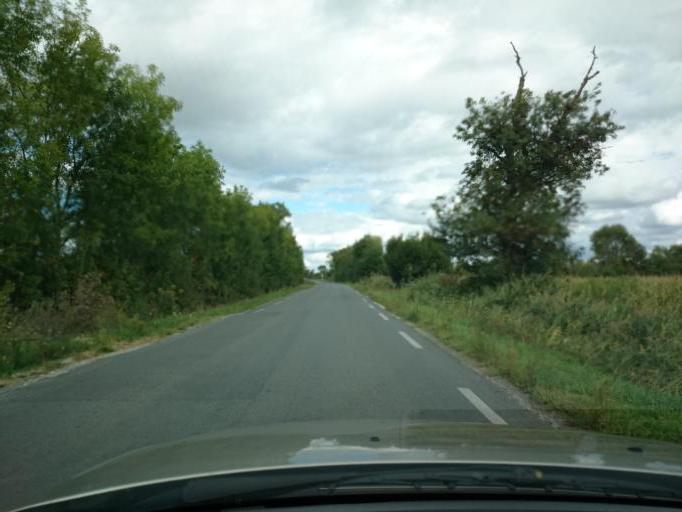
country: FR
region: Aquitaine
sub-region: Departement de la Gironde
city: Saint-Louis-de-Montferrand
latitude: 44.9483
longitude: -0.5566
